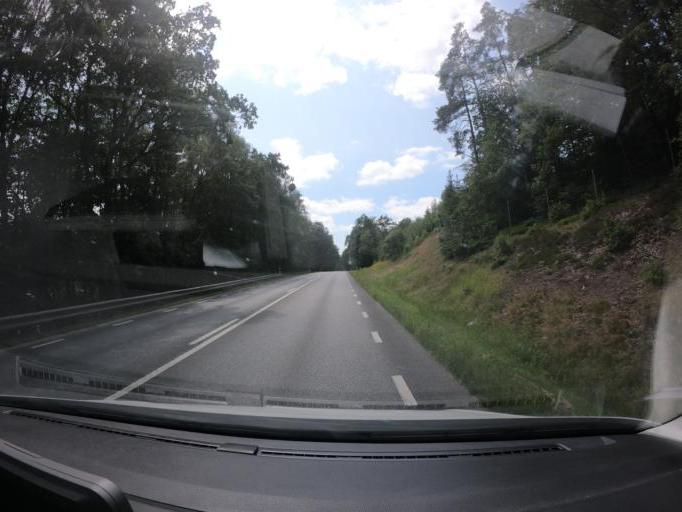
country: SE
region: Skane
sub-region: Hoors Kommun
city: Hoeoer
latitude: 55.9692
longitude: 13.5832
